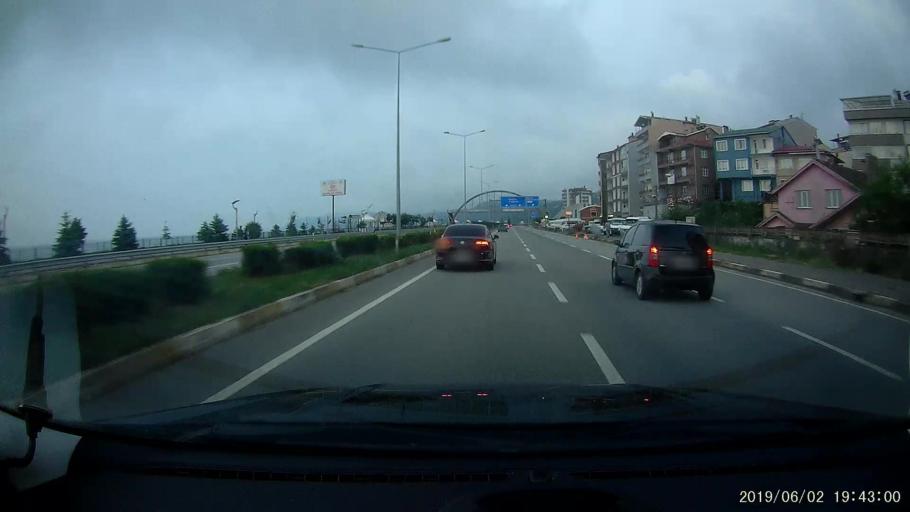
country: TR
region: Giresun
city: Kesap
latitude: 40.9172
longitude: 38.5174
